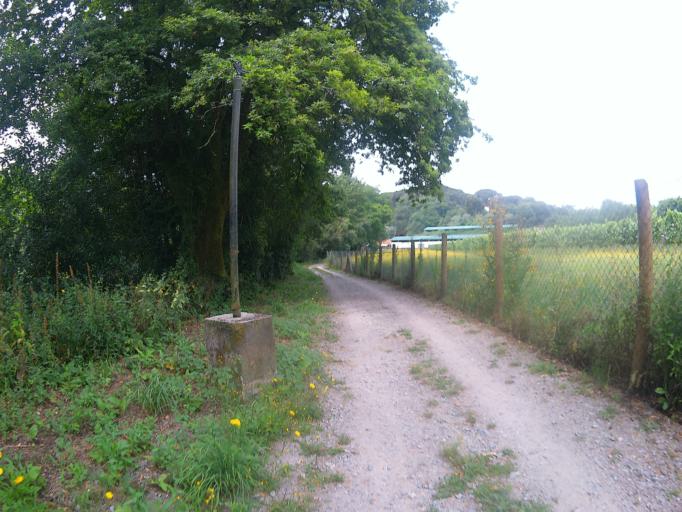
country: PT
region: Viana do Castelo
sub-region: Ponte de Lima
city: Ponte de Lima
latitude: 41.7877
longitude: -8.5187
